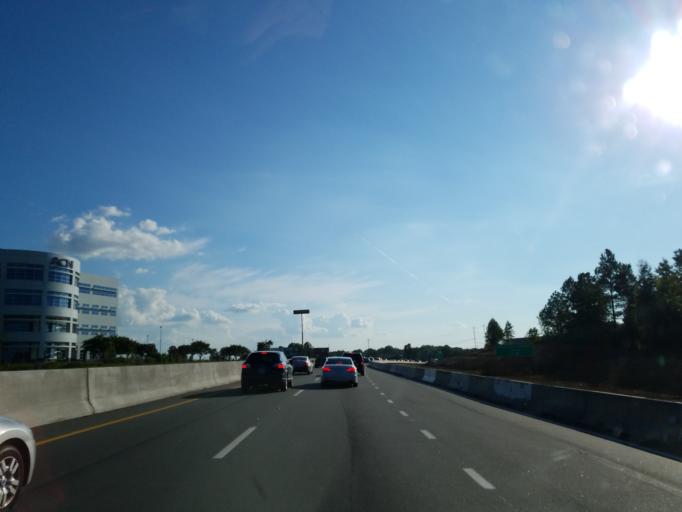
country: US
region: North Carolina
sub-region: Cabarrus County
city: Kannapolis
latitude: 35.4511
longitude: -80.5970
